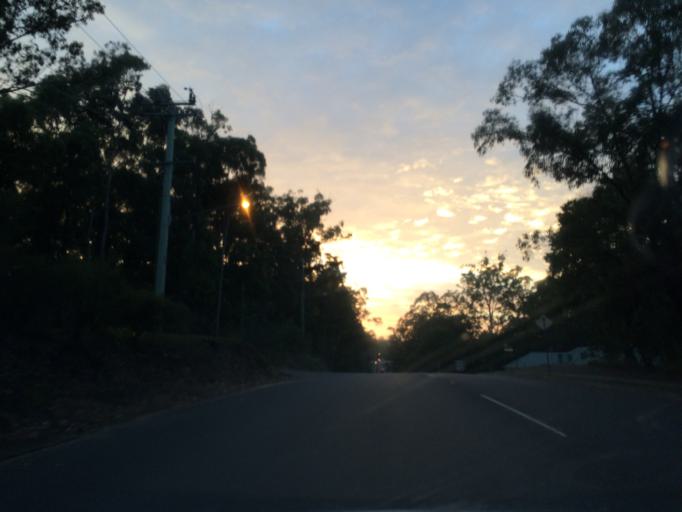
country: AU
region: Queensland
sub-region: Brisbane
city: Kenmore Hills
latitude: -27.4939
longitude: 152.9443
